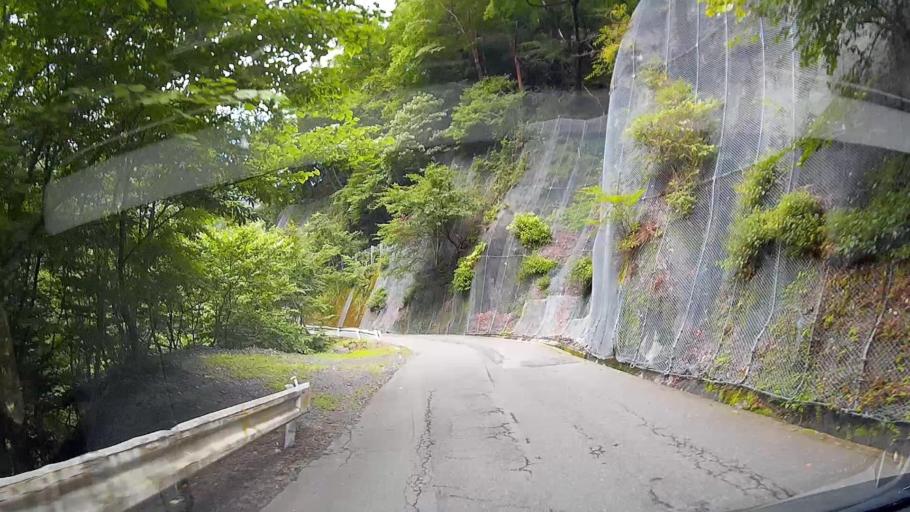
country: JP
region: Shizuoka
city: Shizuoka-shi
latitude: 35.3088
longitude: 138.1856
